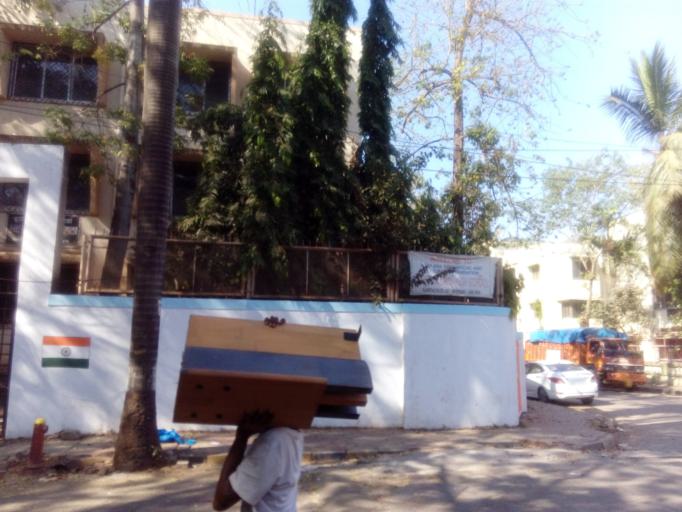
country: IN
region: Maharashtra
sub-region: Mumbai Suburban
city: Mumbai
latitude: 19.0889
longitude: 72.8409
